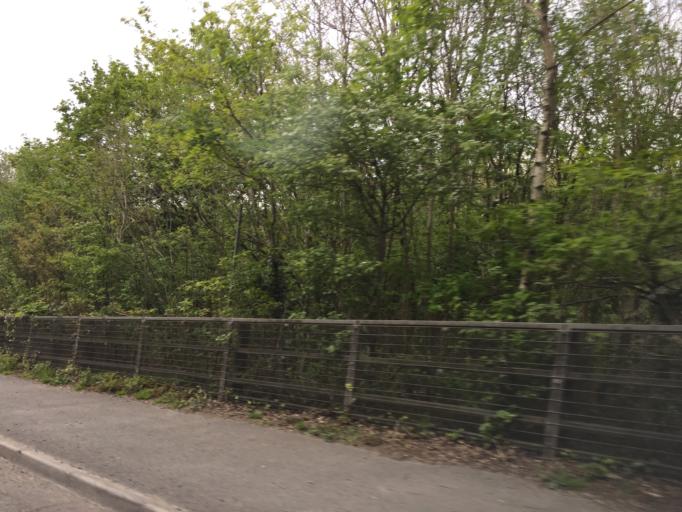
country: GB
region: Wales
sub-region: Merthyr Tydfil County Borough
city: Treharris
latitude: 51.6525
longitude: -3.3092
